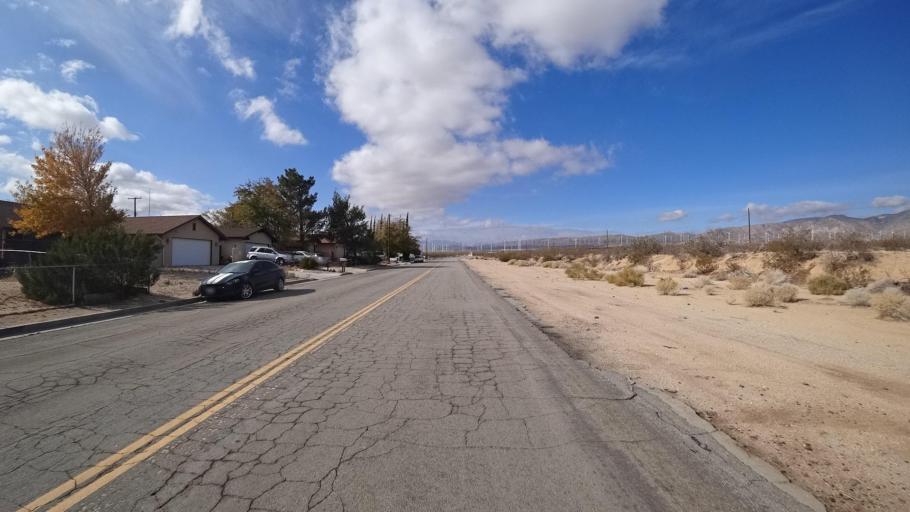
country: US
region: California
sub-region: Kern County
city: Mojave
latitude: 35.0681
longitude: -118.1815
